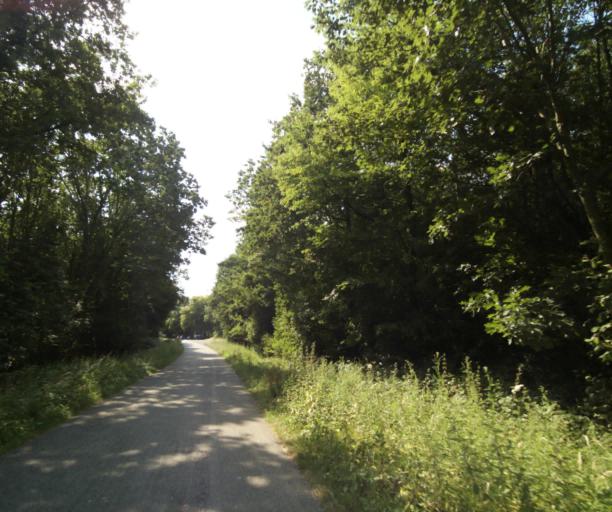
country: FR
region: Lorraine
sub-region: Departement de Meurthe-et-Moselle
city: Chanteheux
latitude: 48.5746
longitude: 6.5417
